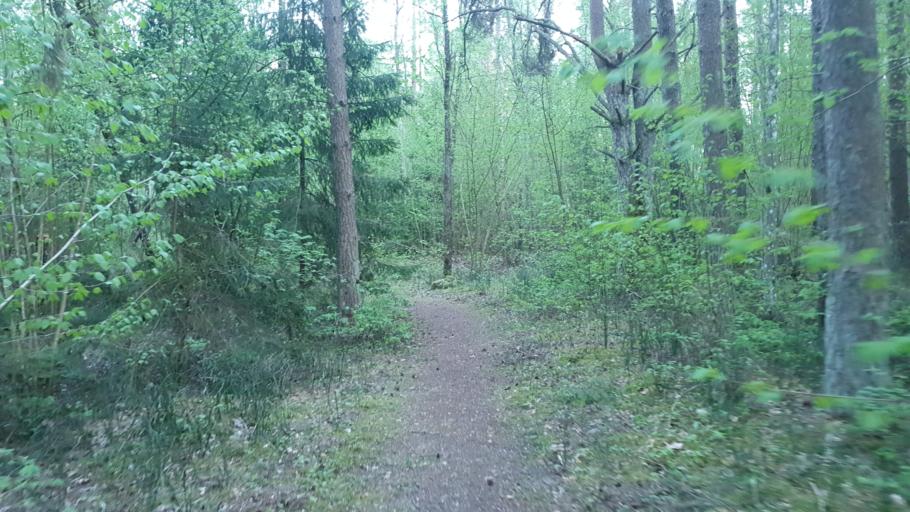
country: LV
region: Ikskile
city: Ikskile
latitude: 56.8354
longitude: 24.4397
